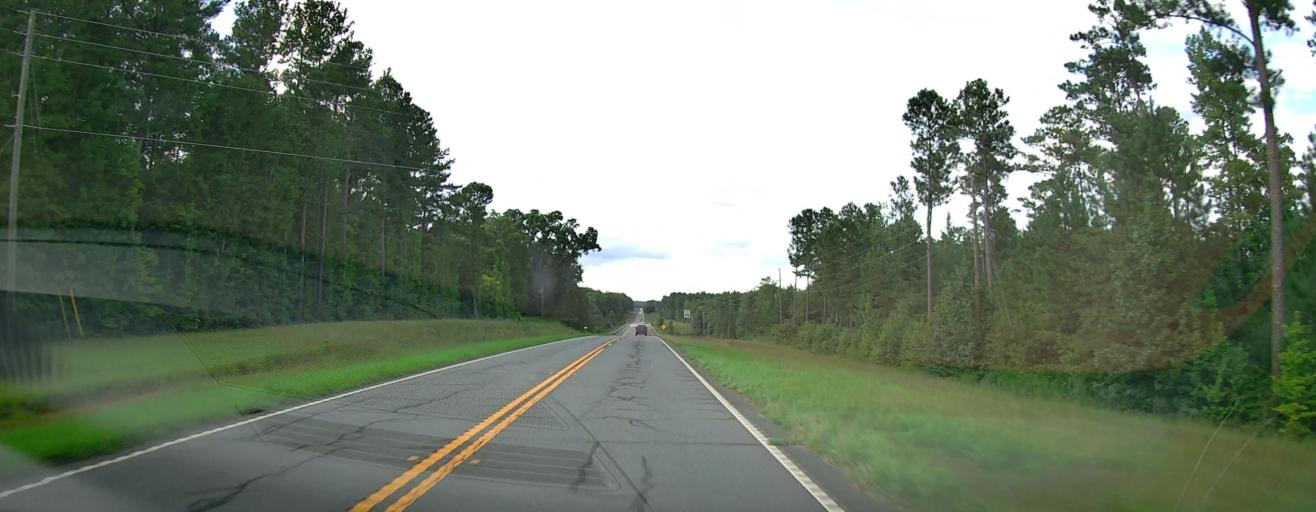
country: US
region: Georgia
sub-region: Meriwether County
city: Greenville
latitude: 33.0410
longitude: -84.5657
